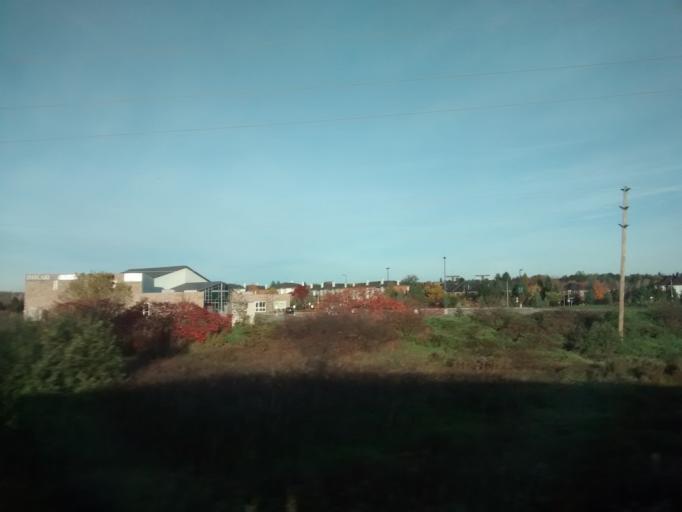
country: CA
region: Ontario
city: Oakville
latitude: 43.4911
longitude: -79.6530
